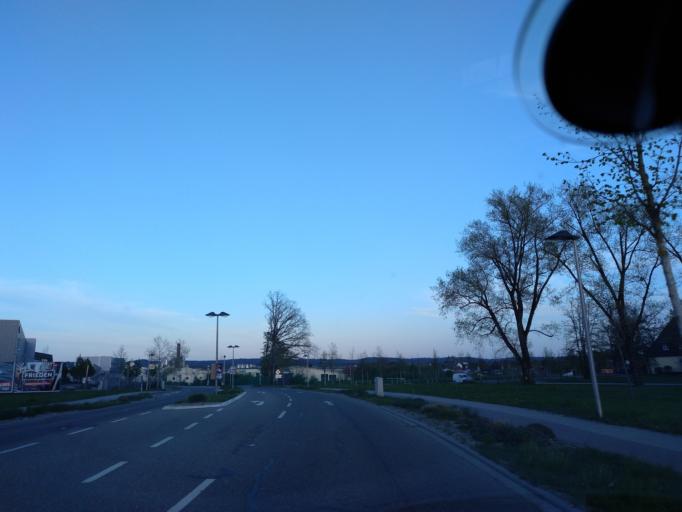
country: DE
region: Baden-Wuerttemberg
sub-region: Regierungsbezirk Stuttgart
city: Crailsheim
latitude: 49.1351
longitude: 10.0545
